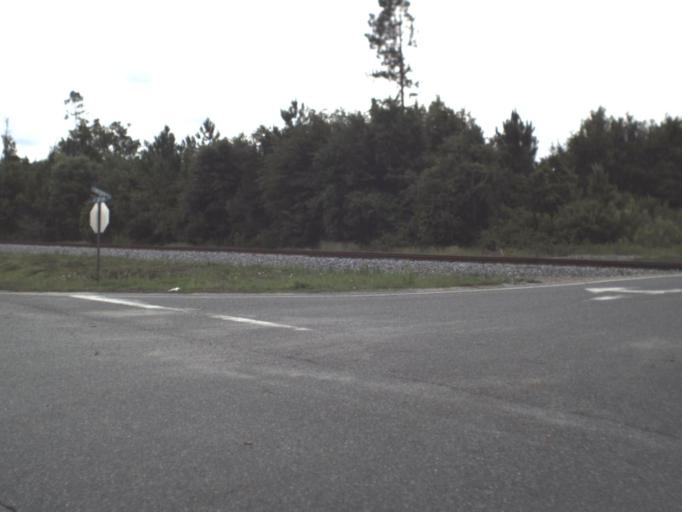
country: US
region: Florida
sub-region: Columbia County
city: Watertown
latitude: 30.1756
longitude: -82.5883
